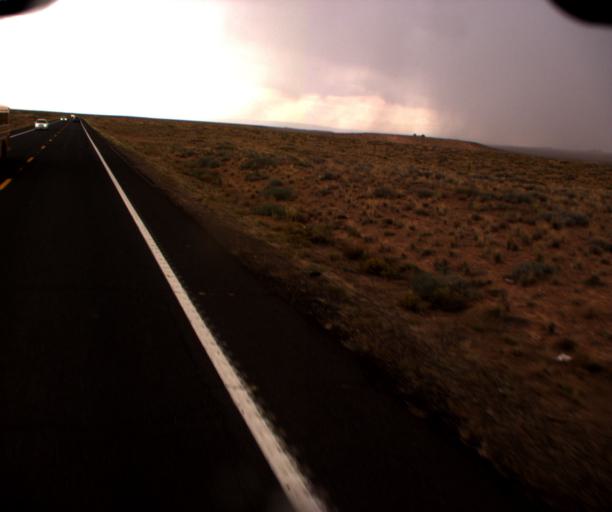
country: US
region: Arizona
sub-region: Coconino County
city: Tuba City
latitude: 36.1760
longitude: -111.0814
